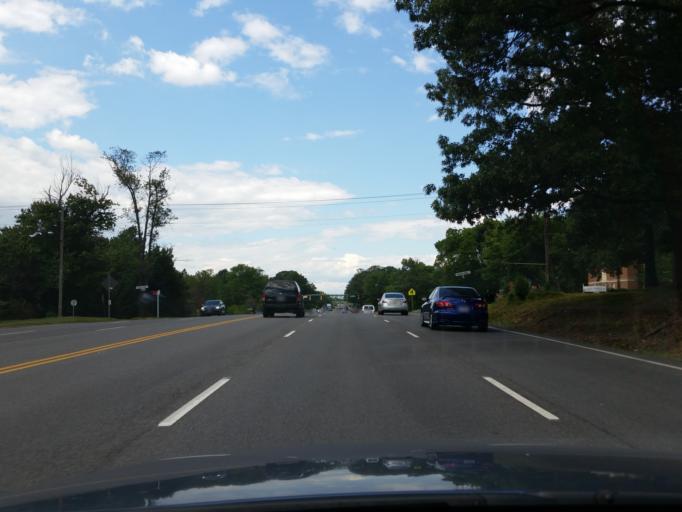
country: US
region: Virginia
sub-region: Arlington County
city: Arlington
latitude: 38.8731
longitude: -77.0913
